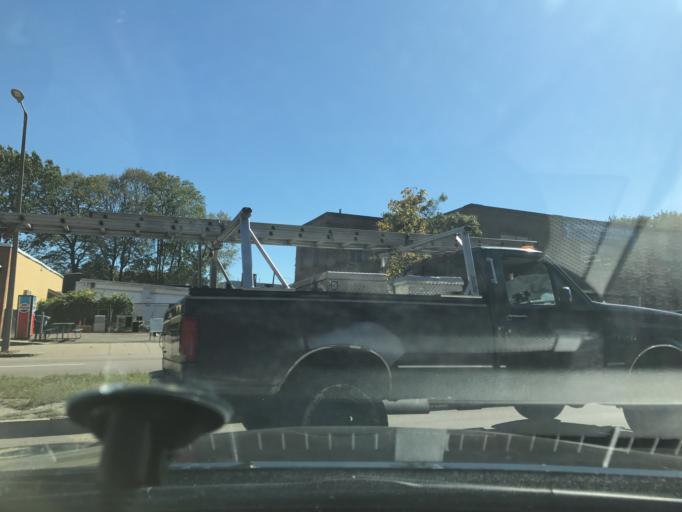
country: US
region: Massachusetts
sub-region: Suffolk County
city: South Boston
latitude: 42.3092
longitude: -71.0741
